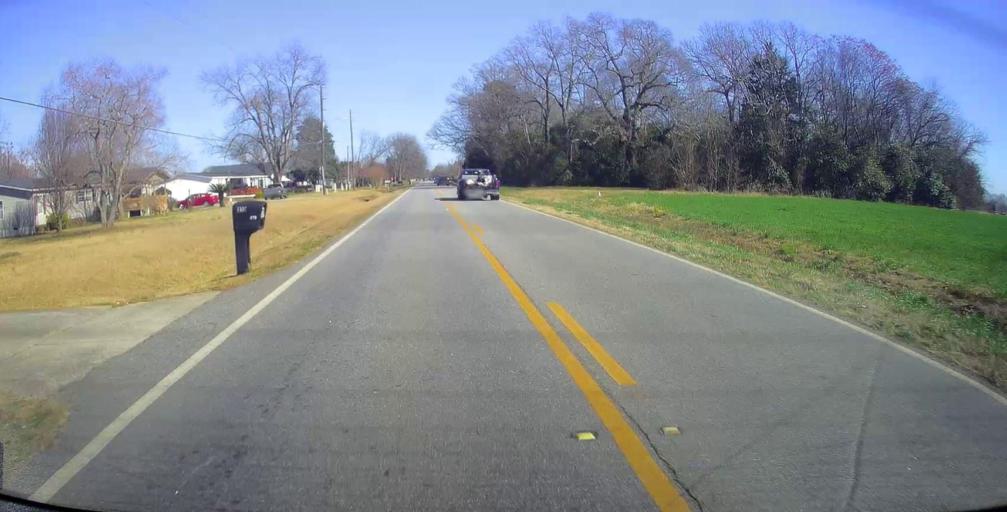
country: US
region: Georgia
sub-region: Houston County
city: Centerville
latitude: 32.6349
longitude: -83.7259
